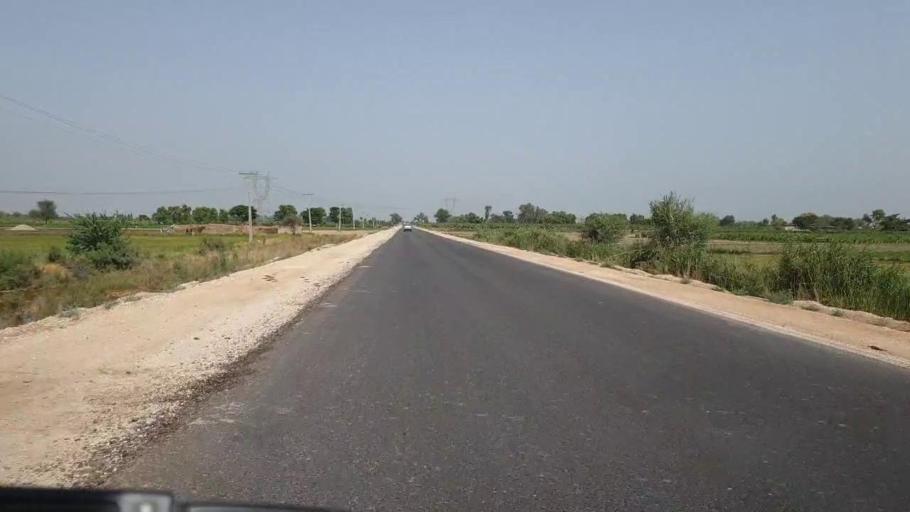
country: PK
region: Sindh
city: Sakrand
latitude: 26.2558
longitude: 68.1961
